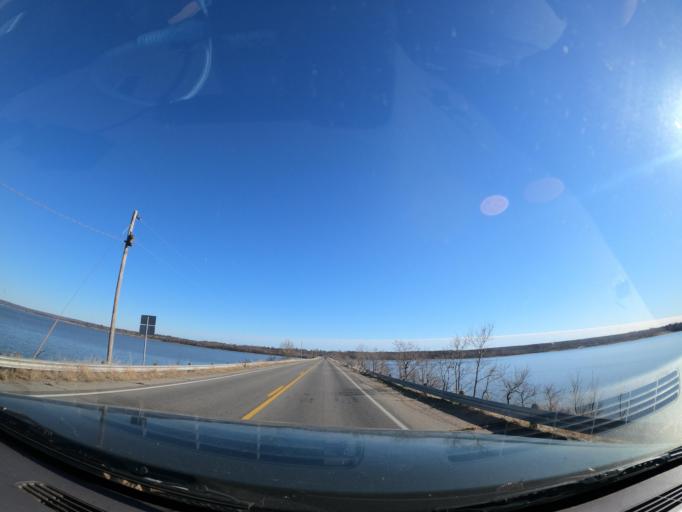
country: US
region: Oklahoma
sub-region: McIntosh County
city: Eufaula
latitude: 35.2445
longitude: -95.5630
